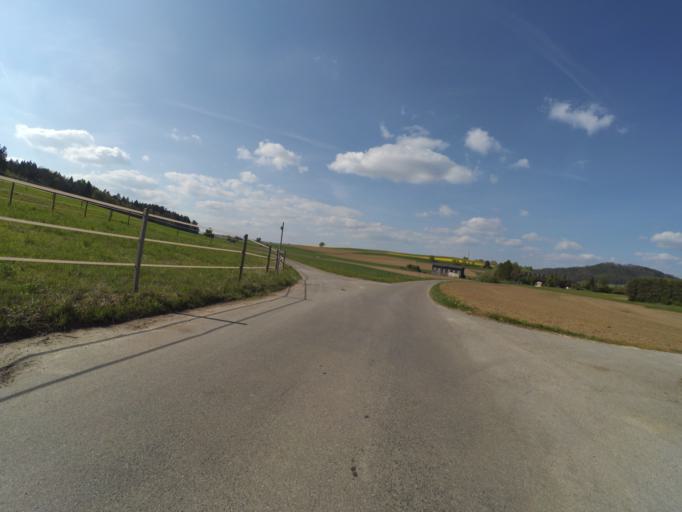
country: CH
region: Thurgau
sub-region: Frauenfeld District
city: Diessenhofen
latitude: 47.6539
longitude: 8.7639
